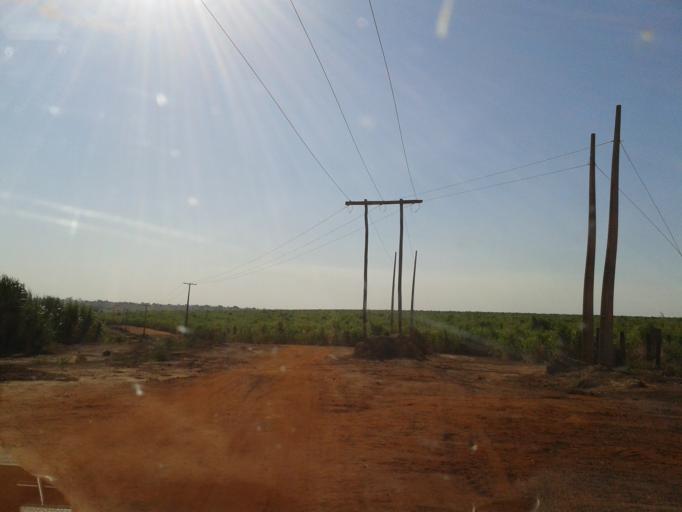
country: BR
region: Minas Gerais
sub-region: Santa Vitoria
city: Santa Vitoria
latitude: -18.7304
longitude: -50.2664
